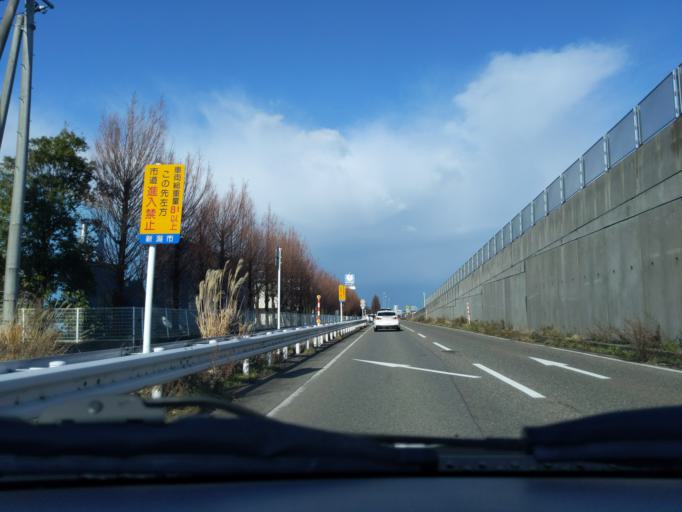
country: JP
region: Niigata
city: Kameda-honcho
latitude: 37.8706
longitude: 139.0870
